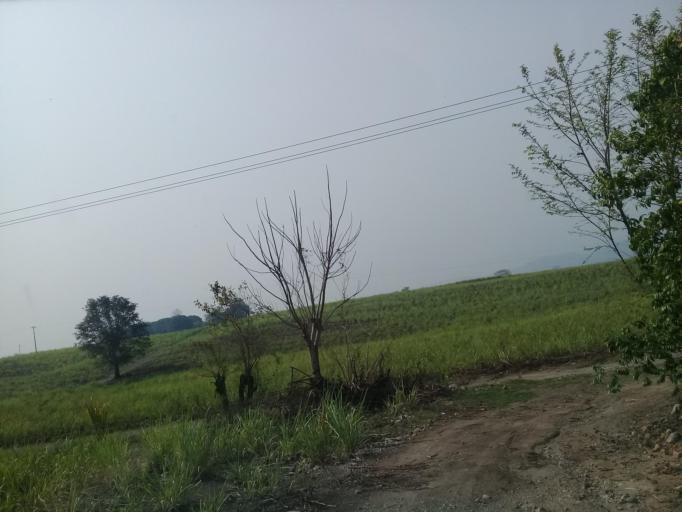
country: MX
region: Oaxaca
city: Acatlan de Perez Figueroa
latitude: 18.6084
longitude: -96.5725
